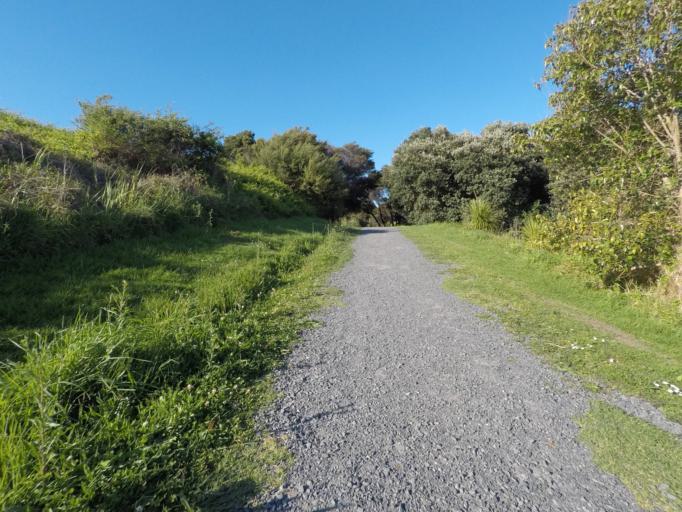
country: NZ
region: Auckland
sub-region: Auckland
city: Rosebank
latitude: -36.8410
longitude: 174.6596
